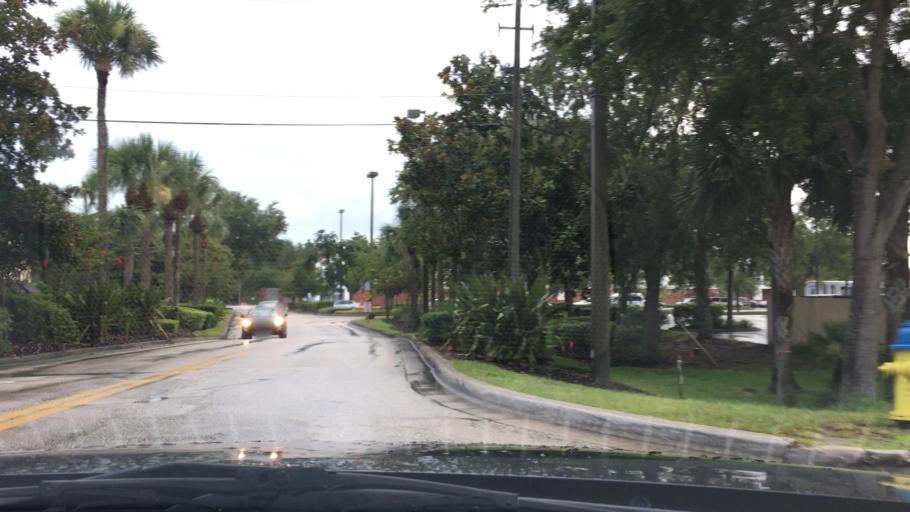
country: US
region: Florida
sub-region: Volusia County
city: Ormond Beach
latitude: 29.2592
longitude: -81.1103
